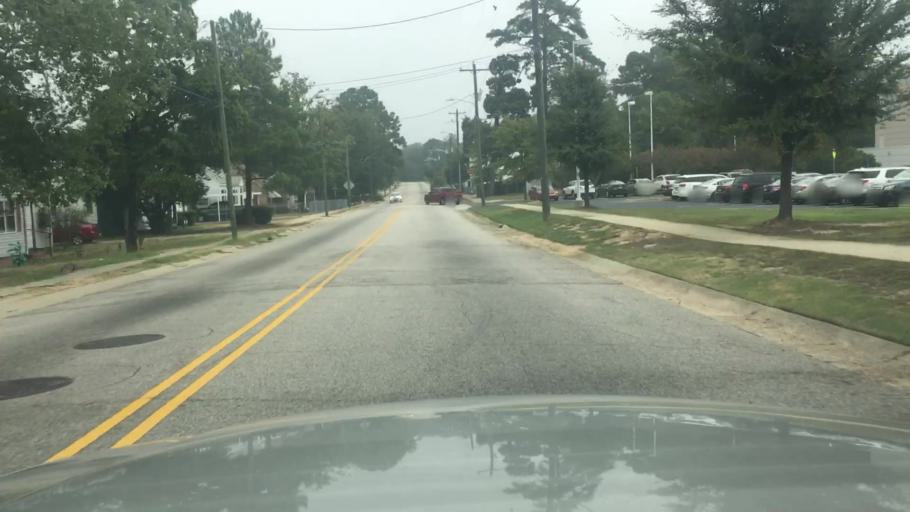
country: US
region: North Carolina
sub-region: Cumberland County
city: Fayetteville
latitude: 35.0730
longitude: -78.8833
